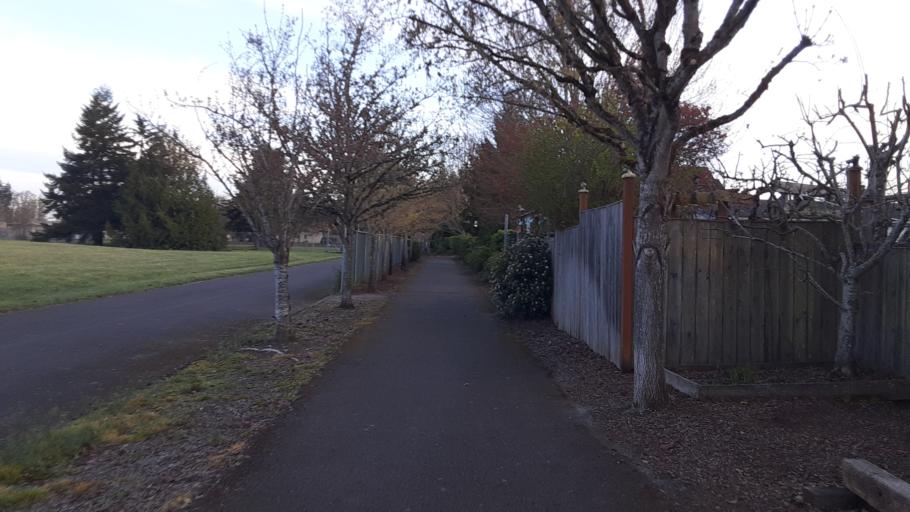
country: US
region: Oregon
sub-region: Benton County
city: Corvallis
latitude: 44.5367
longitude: -123.2539
